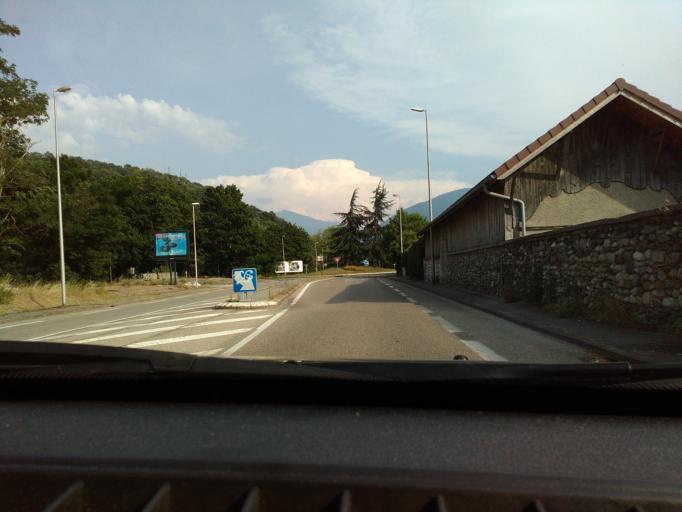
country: FR
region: Rhone-Alpes
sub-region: Departement de l'Isere
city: Le Pont-de-Claix
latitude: 45.1153
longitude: 5.7047
